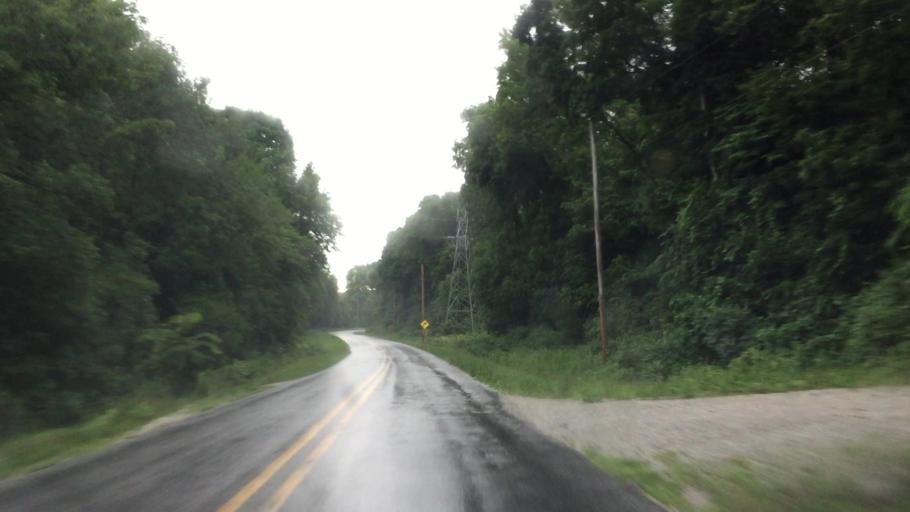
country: US
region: Iowa
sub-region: Lee County
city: Fort Madison
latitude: 40.6090
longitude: -91.2801
